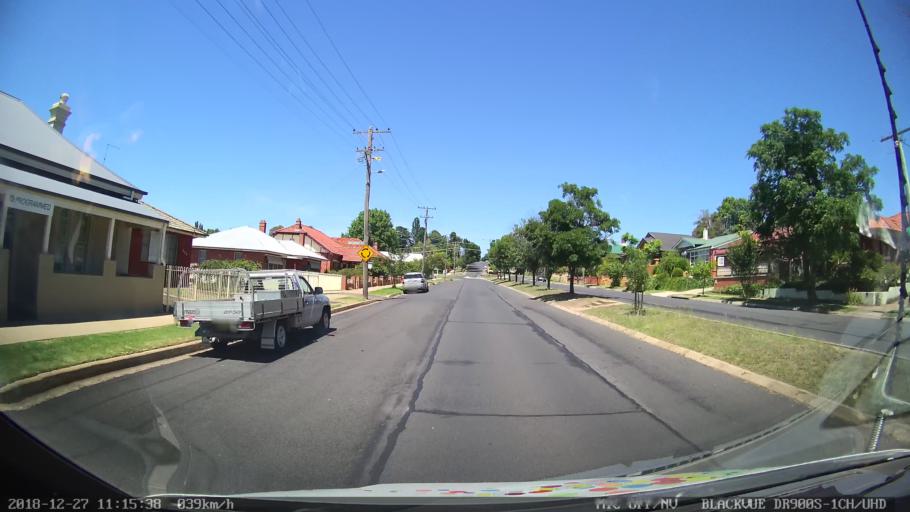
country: AU
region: New South Wales
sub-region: Bathurst Regional
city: Bathurst
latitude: -33.4233
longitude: 149.5731
